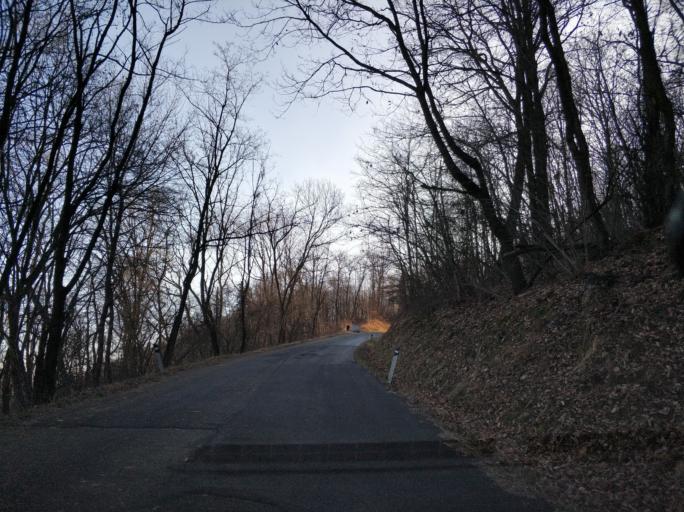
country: IT
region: Piedmont
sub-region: Provincia di Torino
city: Vauda Canavese Superiore
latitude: 45.2680
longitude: 7.6376
